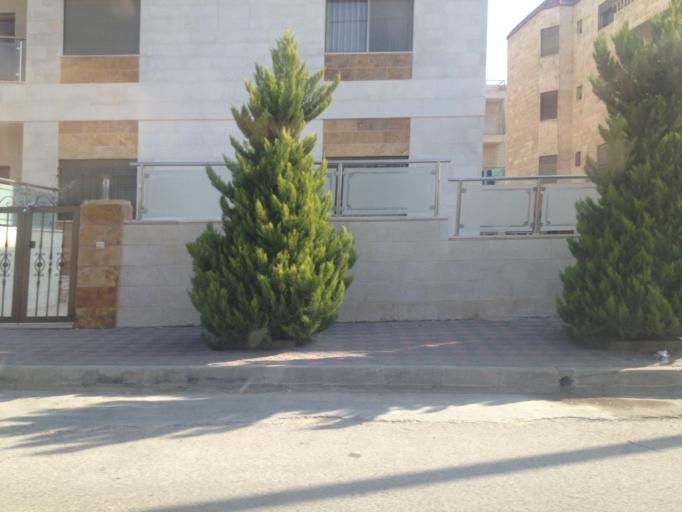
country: JO
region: Amman
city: Wadi as Sir
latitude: 31.9509
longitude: 35.8570
